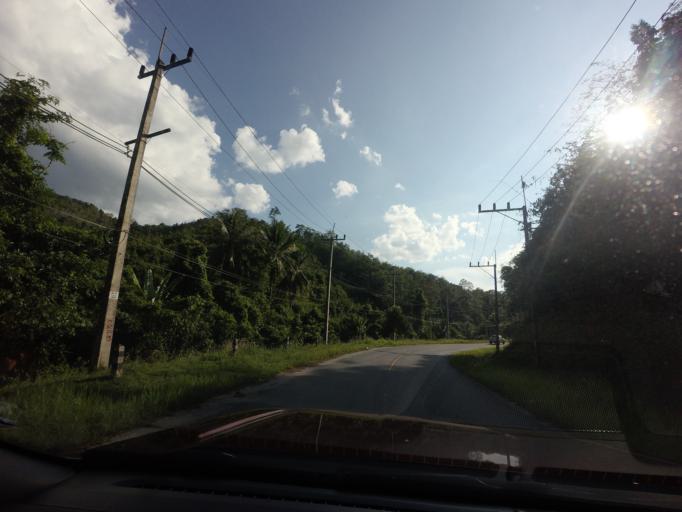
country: TH
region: Yala
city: Than To
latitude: 6.1924
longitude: 101.2477
